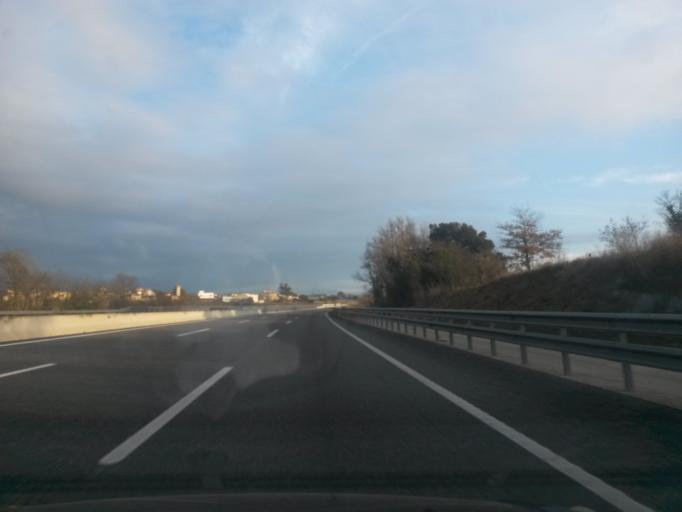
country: ES
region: Catalonia
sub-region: Provincia de Girona
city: Vilafant
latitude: 42.2414
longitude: 2.9380
